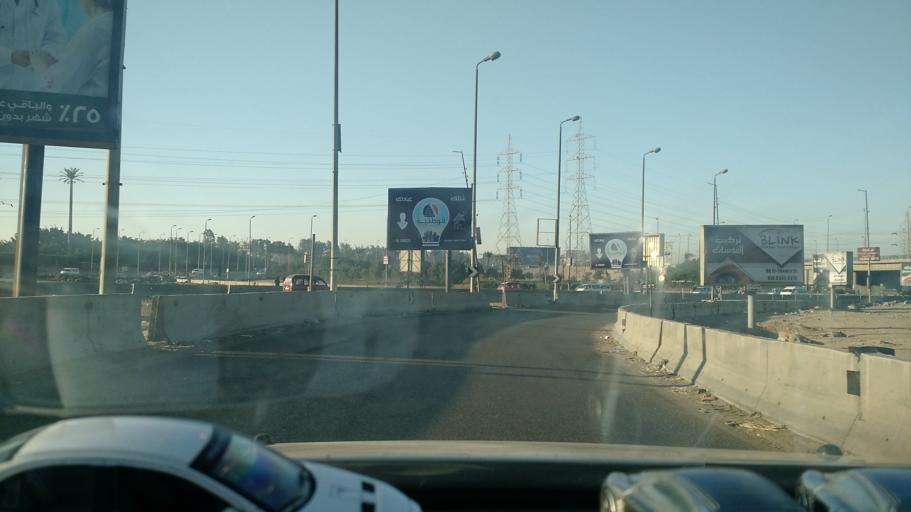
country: EG
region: Muhafazat al Qalyubiyah
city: Al Khankah
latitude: 30.0805
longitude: 31.4378
